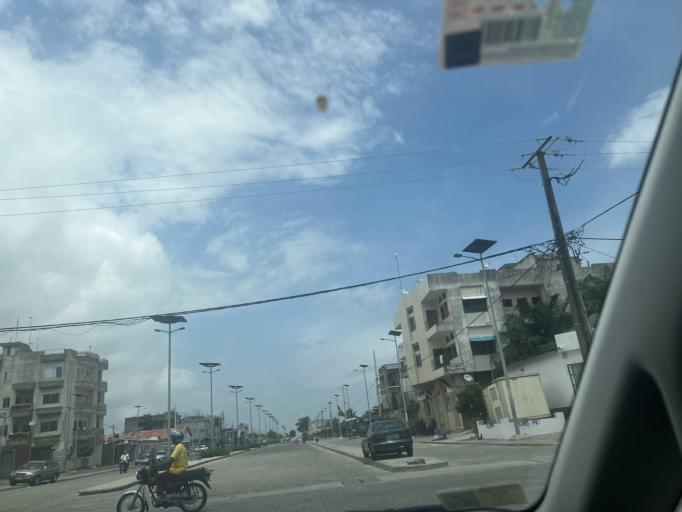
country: BJ
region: Littoral
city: Cotonou
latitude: 6.3885
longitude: 2.4469
